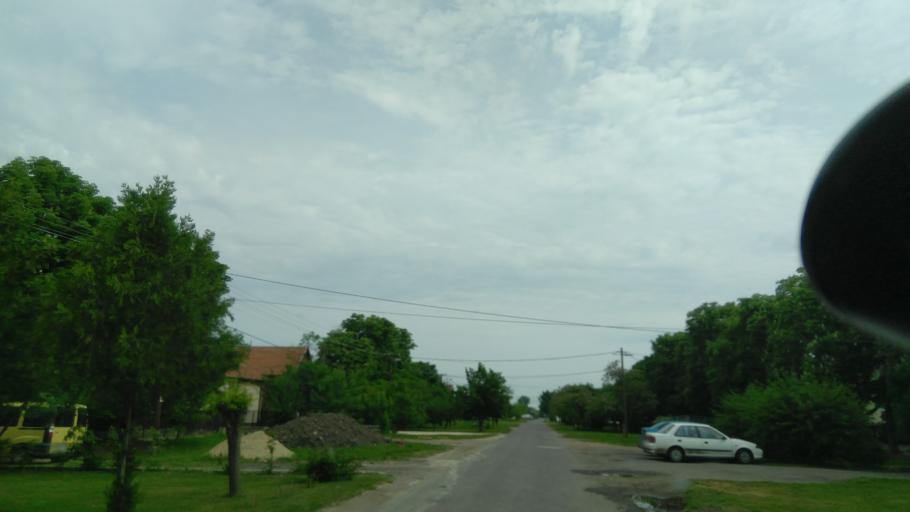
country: HU
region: Bekes
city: Szeghalom
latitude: 47.0189
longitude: 21.1675
